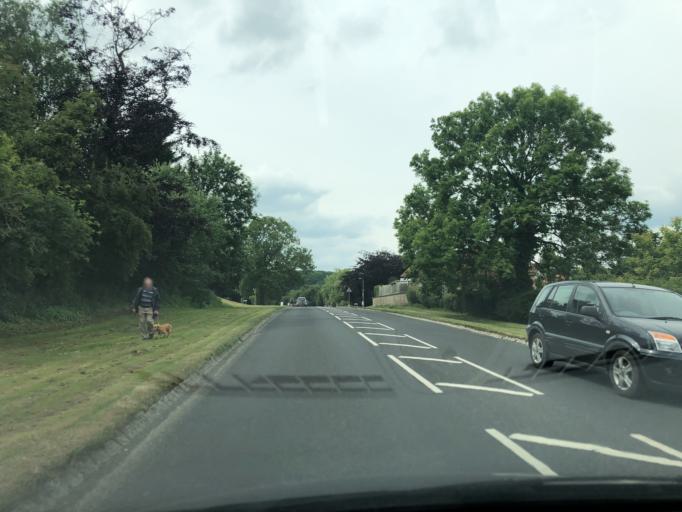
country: GB
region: England
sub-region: North Yorkshire
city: Helmsley
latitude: 54.2669
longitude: -0.9342
